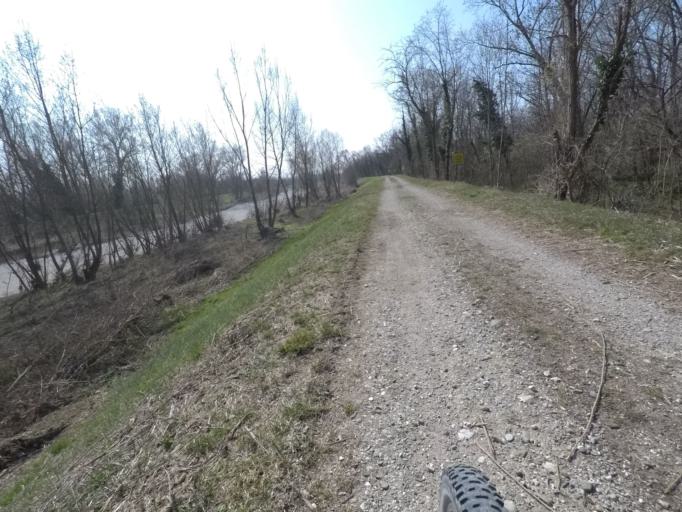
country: IT
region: Friuli Venezia Giulia
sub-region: Provincia di Udine
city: Remanzacco
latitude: 46.0574
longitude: 13.3263
